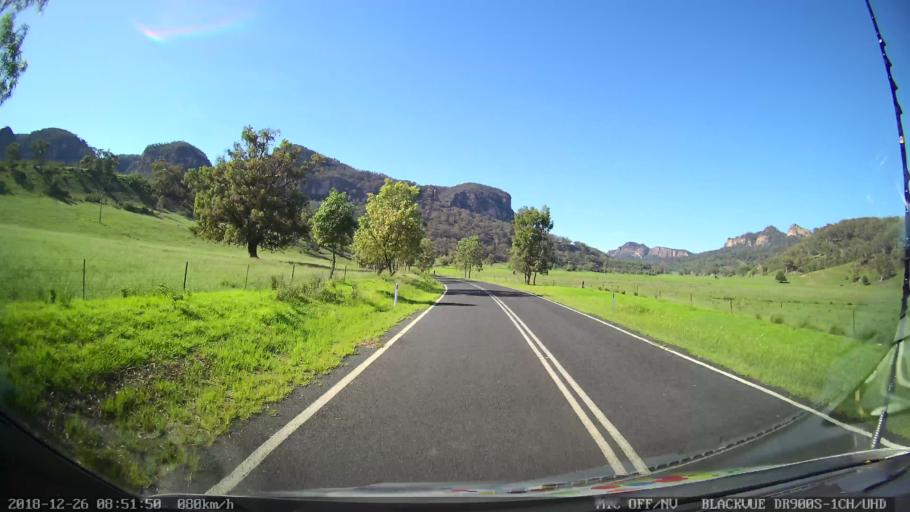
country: AU
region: New South Wales
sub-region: Mid-Western Regional
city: Kandos
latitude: -32.5899
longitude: 150.0880
